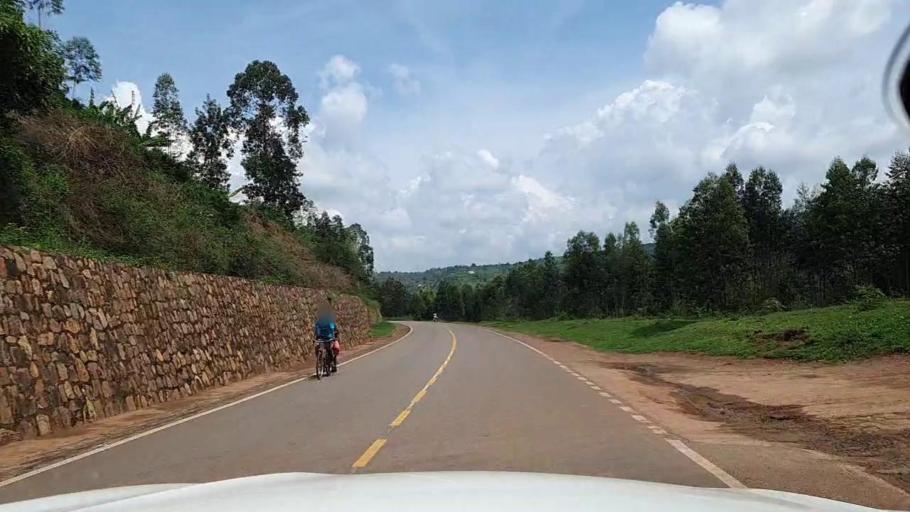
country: RW
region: Kigali
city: Kigali
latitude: -1.8558
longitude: 30.0970
